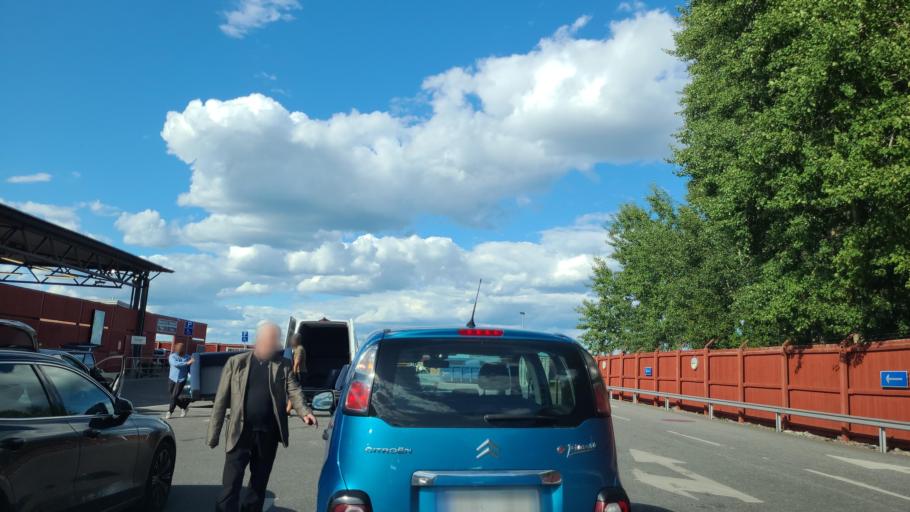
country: SE
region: Stockholm
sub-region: Stockholms Kommun
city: Bromma
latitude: 59.3487
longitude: 17.9499
